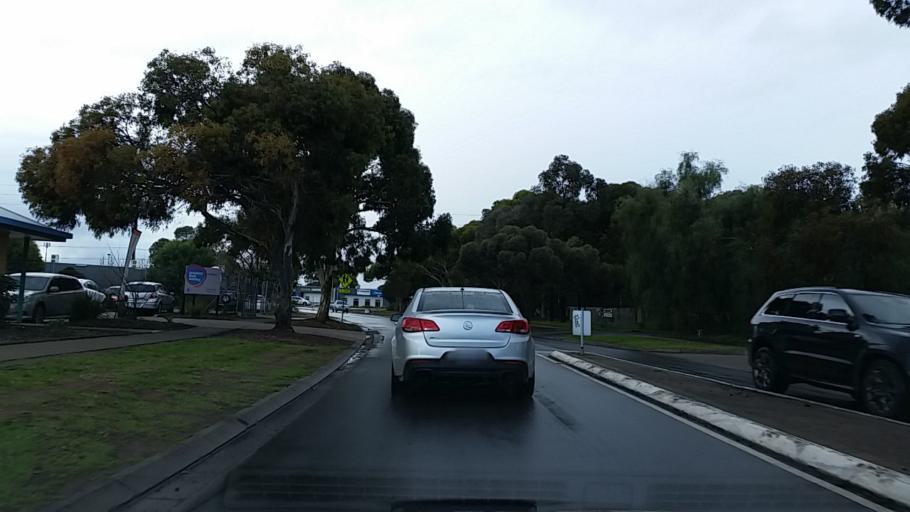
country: AU
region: South Australia
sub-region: Playford
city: Smithfield
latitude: -34.6832
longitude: 138.6881
